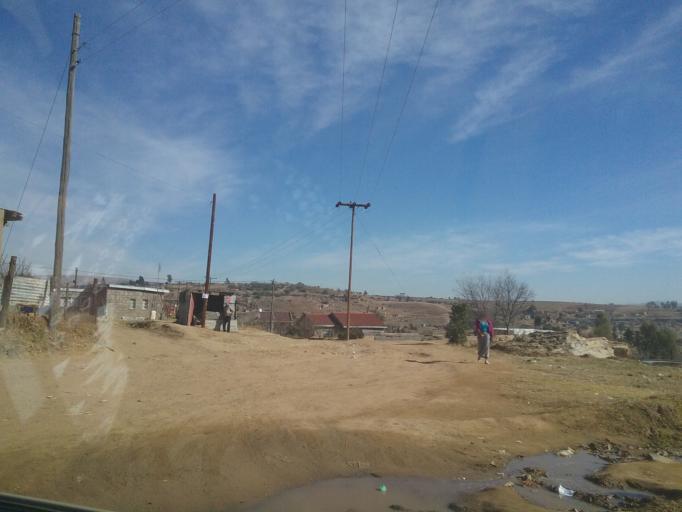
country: LS
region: Maseru
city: Maseru
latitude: -29.4183
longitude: 27.5549
